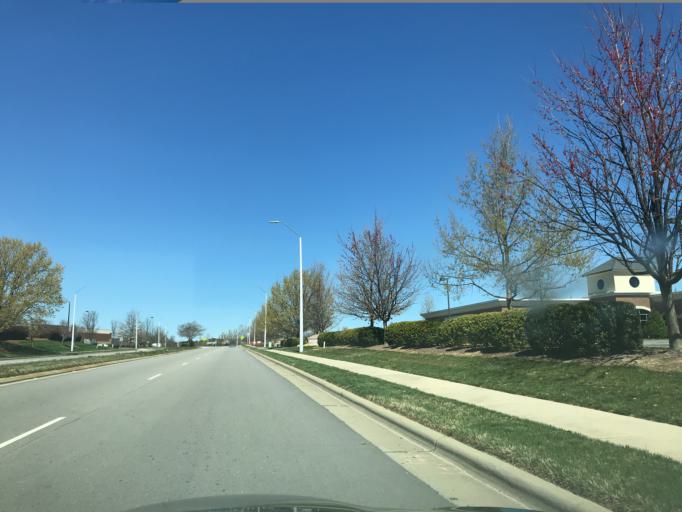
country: US
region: North Carolina
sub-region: Wake County
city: Garner
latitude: 35.6860
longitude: -78.5752
